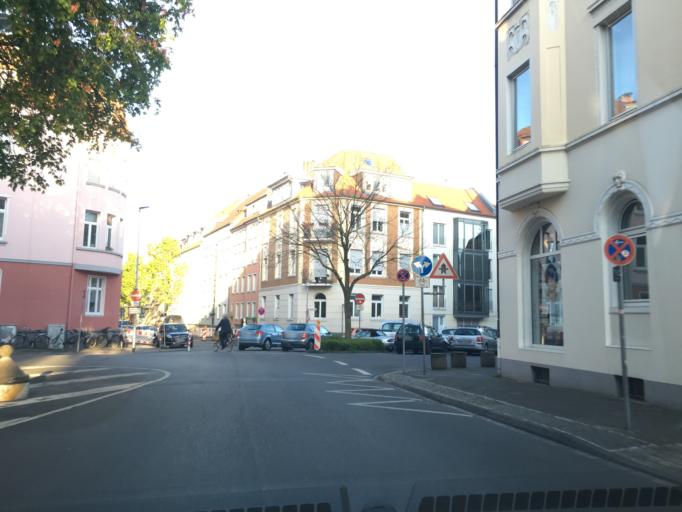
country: DE
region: North Rhine-Westphalia
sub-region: Regierungsbezirk Munster
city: Muenster
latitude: 51.9725
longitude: 7.6289
